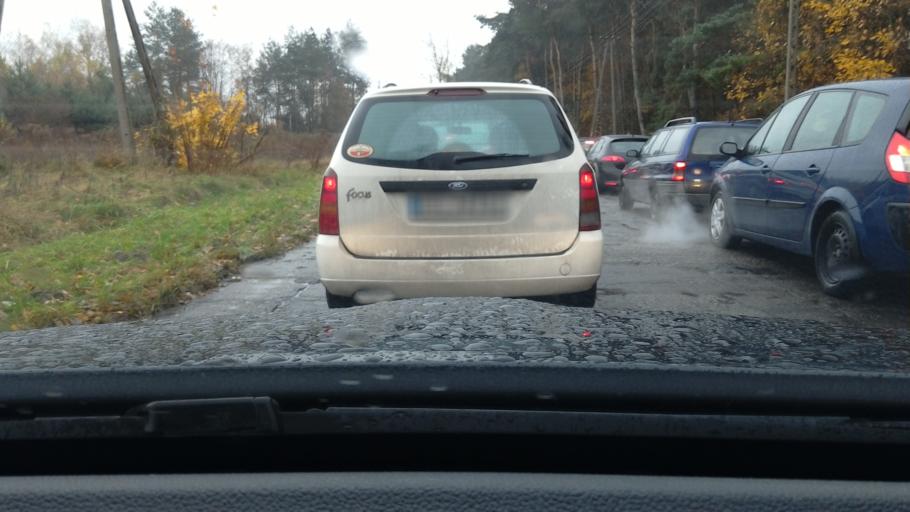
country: PL
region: Lodz Voivodeship
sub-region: Skierniewice
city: Skierniewice
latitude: 51.9388
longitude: 20.1560
